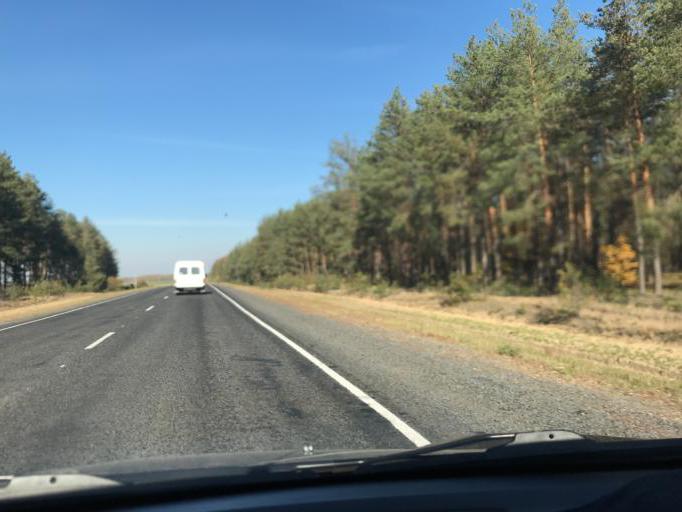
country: BY
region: Gomel
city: Parychy
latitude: 52.6903
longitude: 29.3645
